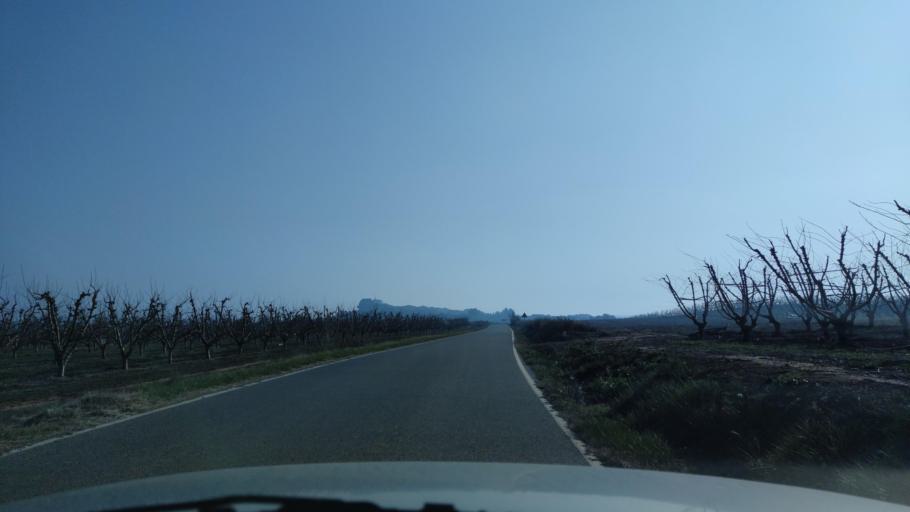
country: ES
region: Catalonia
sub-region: Provincia de Lleida
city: Sunyer
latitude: 41.5285
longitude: 0.5827
